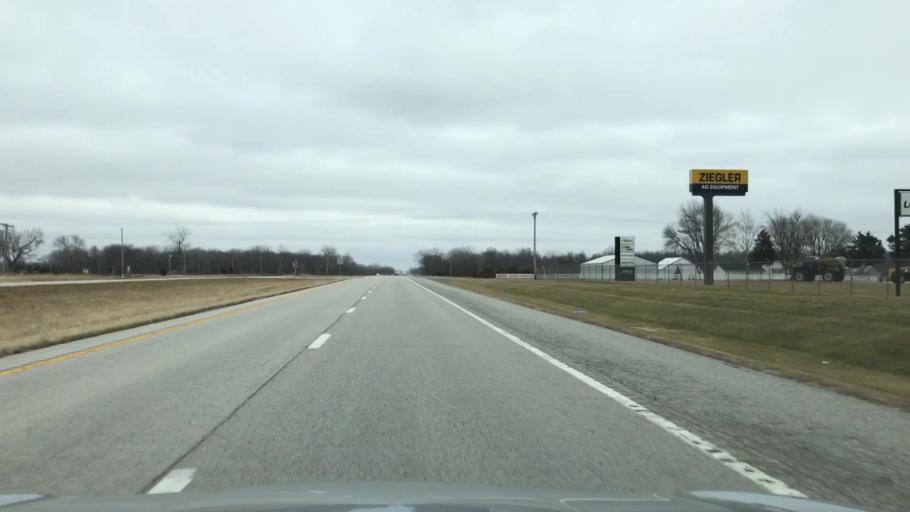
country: US
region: Missouri
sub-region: Livingston County
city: Chillicothe
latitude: 39.7767
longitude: -93.4457
